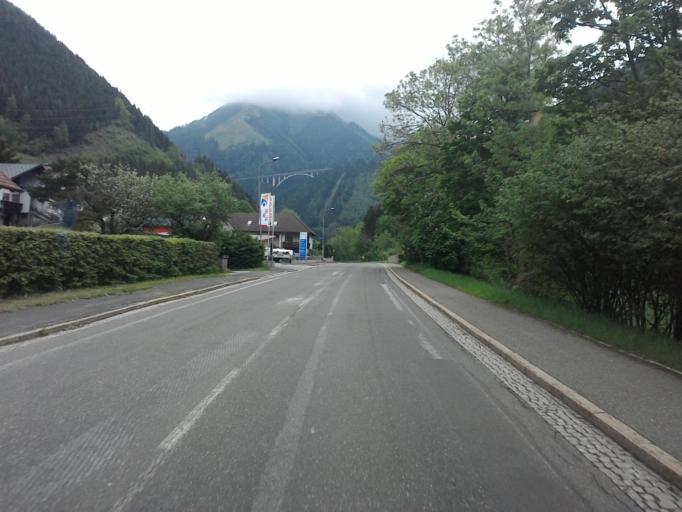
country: AT
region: Styria
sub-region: Politischer Bezirk Leoben
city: Eisenerz
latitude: 47.5415
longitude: 14.9064
